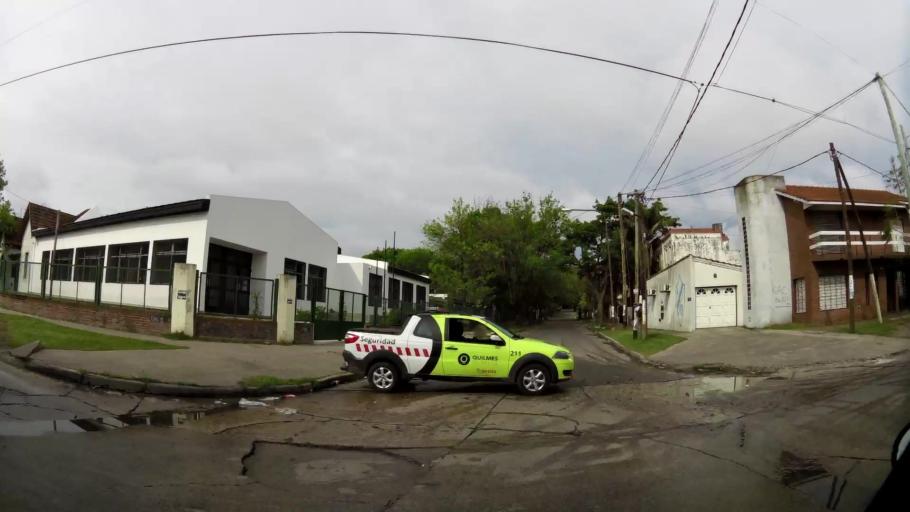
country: AR
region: Buenos Aires
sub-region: Partido de Quilmes
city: Quilmes
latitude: -34.7188
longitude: -58.2449
